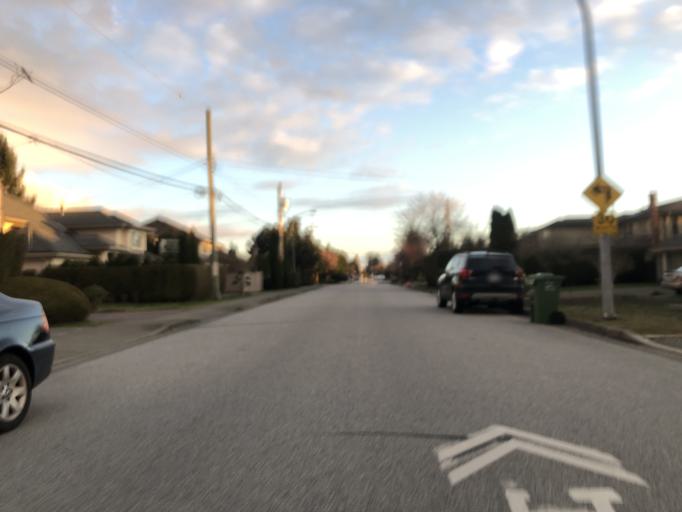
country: CA
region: British Columbia
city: Richmond
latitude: 49.1527
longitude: -123.1198
